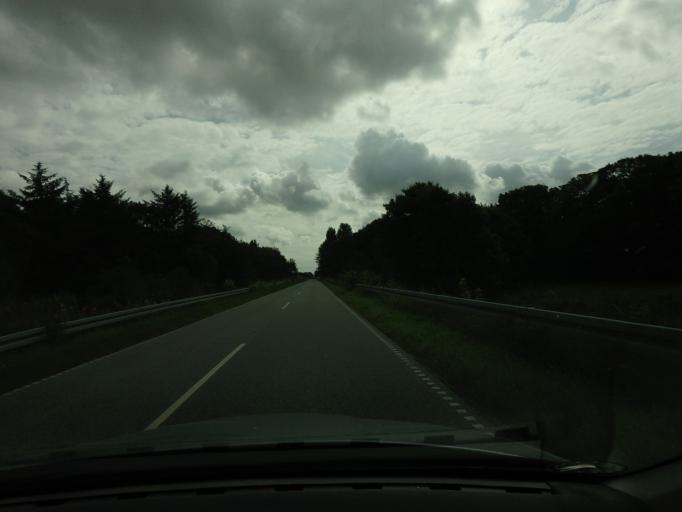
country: DK
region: North Denmark
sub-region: Bronderslev Kommune
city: Dronninglund
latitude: 57.2865
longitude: 10.3216
